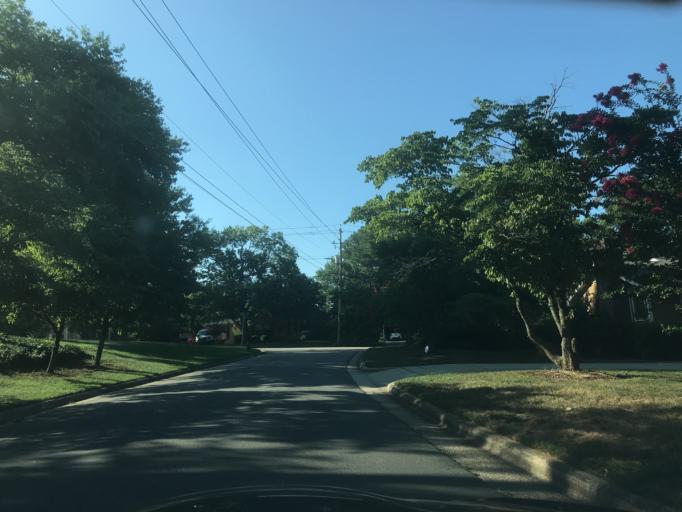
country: US
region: North Carolina
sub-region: Wake County
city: West Raleigh
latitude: 35.8501
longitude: -78.6292
